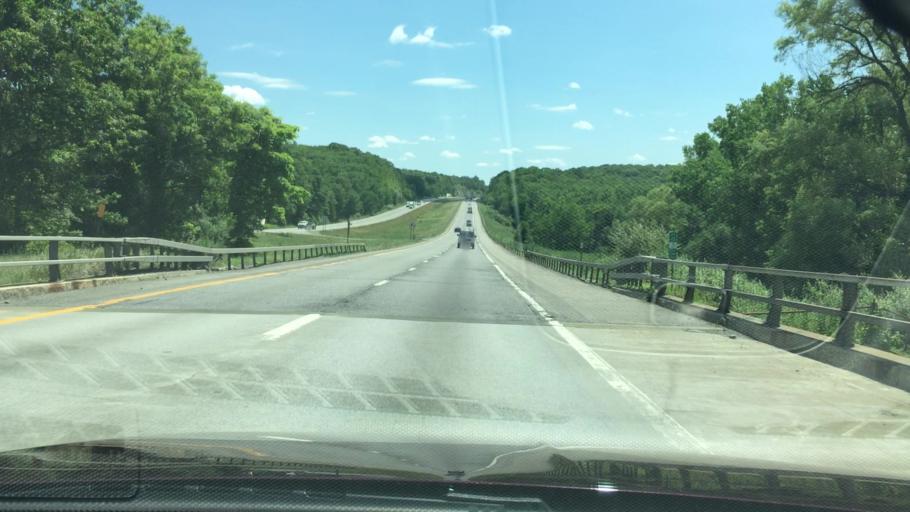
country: US
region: New York
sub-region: Putnam County
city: Lake Carmel
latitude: 41.4512
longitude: -73.6385
